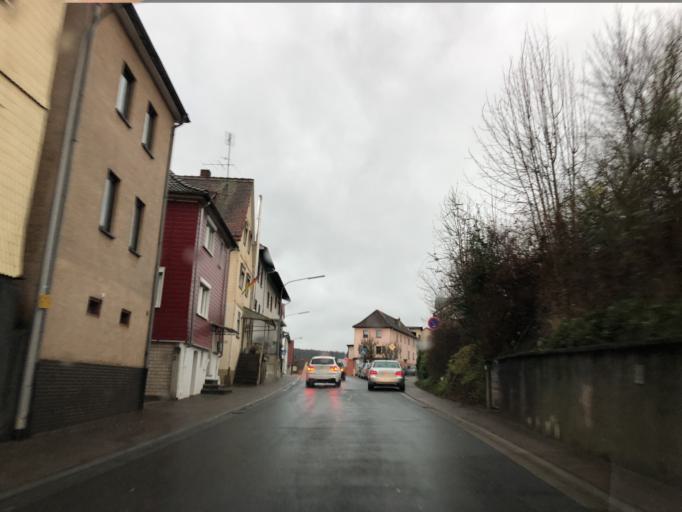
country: DE
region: Hesse
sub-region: Regierungsbezirk Darmstadt
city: Bad Konig
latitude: 49.7434
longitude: 9.0077
